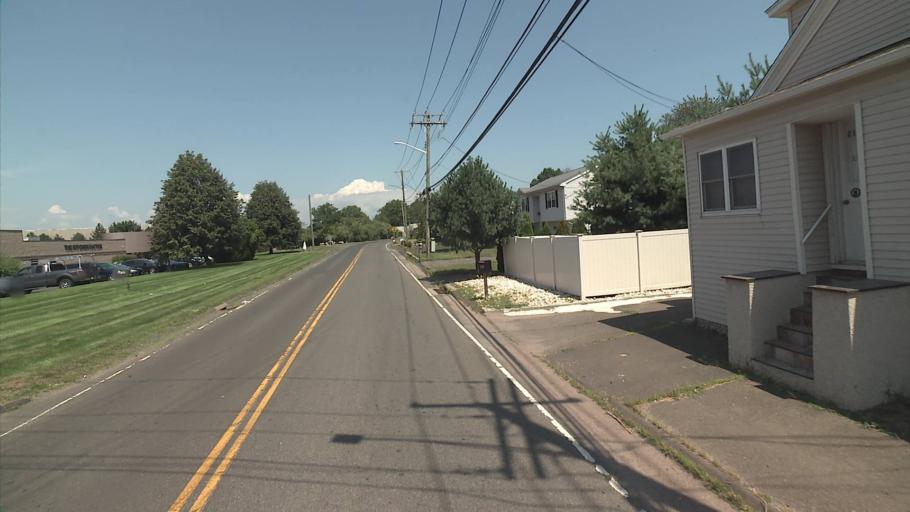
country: US
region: Connecticut
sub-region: New Haven County
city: East Haven
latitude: 41.2596
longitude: -72.8744
